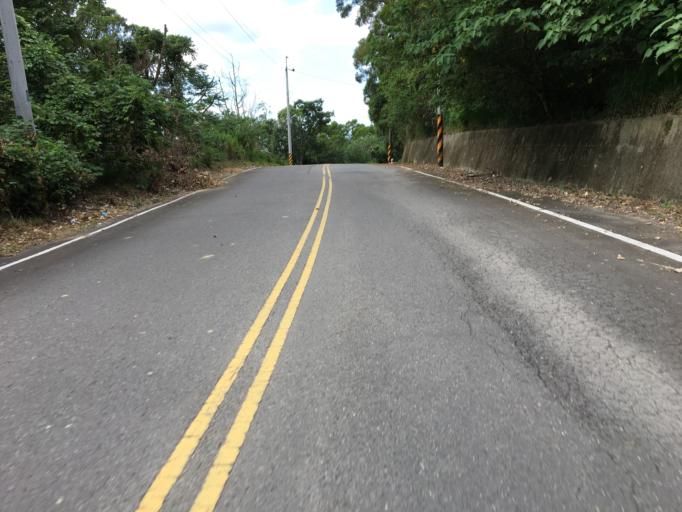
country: TW
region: Taiwan
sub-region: Hsinchu
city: Hsinchu
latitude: 24.7097
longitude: 120.9540
